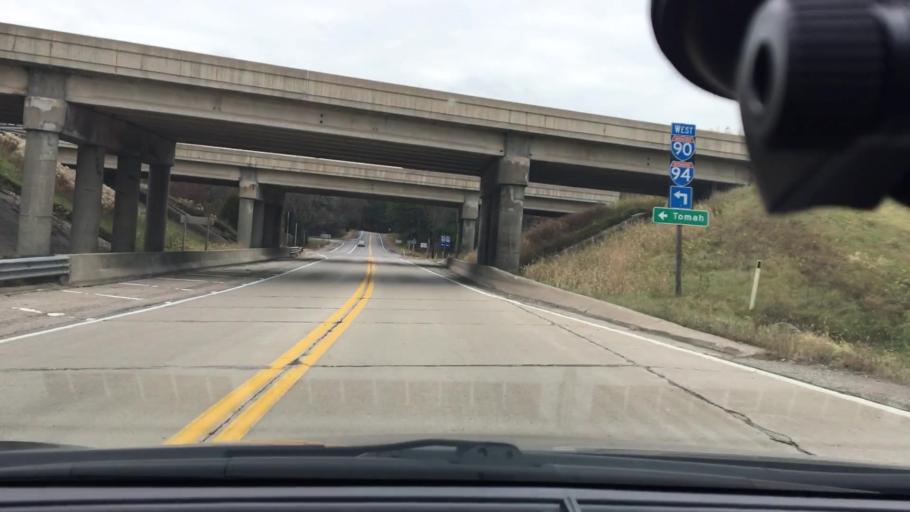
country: US
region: Wisconsin
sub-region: Columbia County
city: Wisconsin Dells
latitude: 43.6499
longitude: -89.8138
